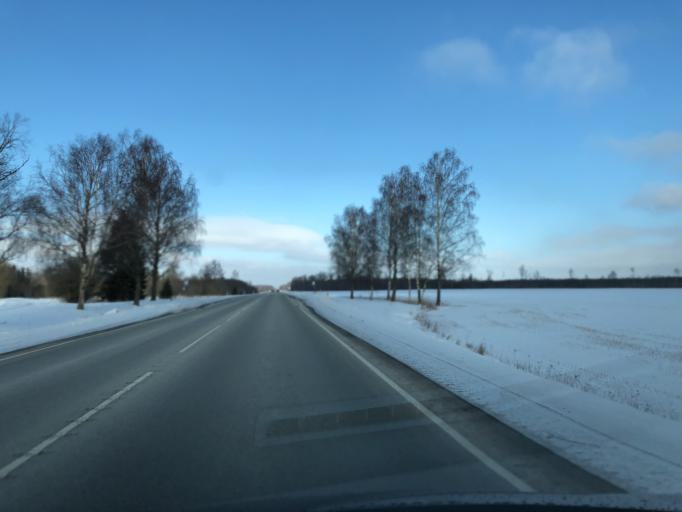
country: EE
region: Jaervamaa
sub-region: Paide linn
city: Paide
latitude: 58.7877
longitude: 25.7583
